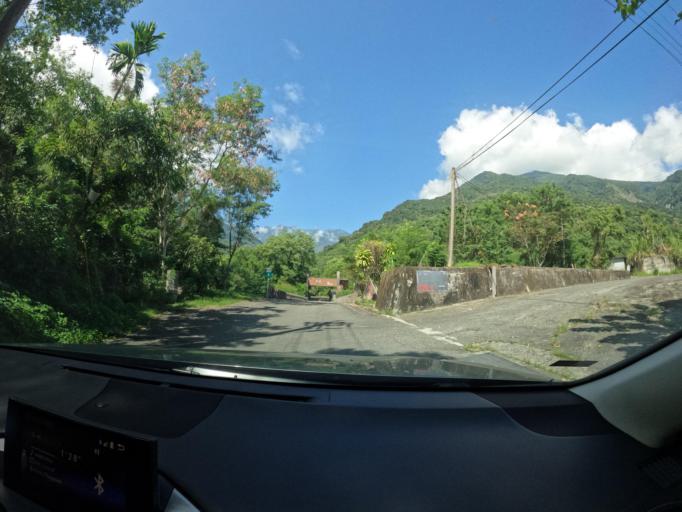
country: TW
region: Taiwan
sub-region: Hualien
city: Hualian
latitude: 23.5887
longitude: 121.3558
